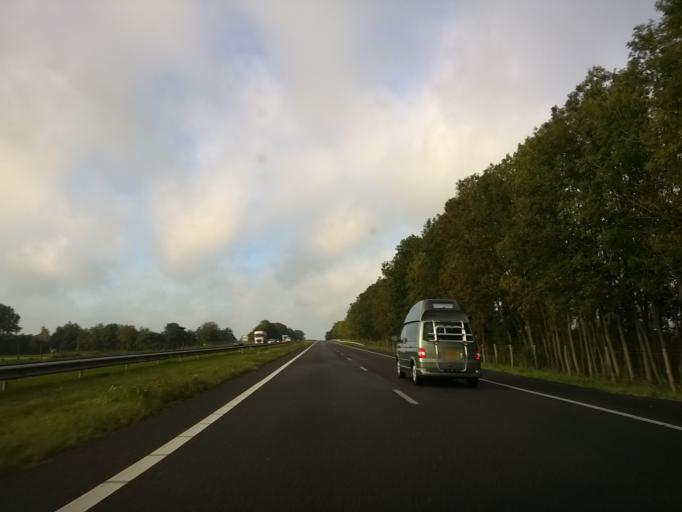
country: NL
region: Groningen
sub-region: Gemeente Grootegast
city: Grootegast
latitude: 53.1475
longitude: 6.2476
